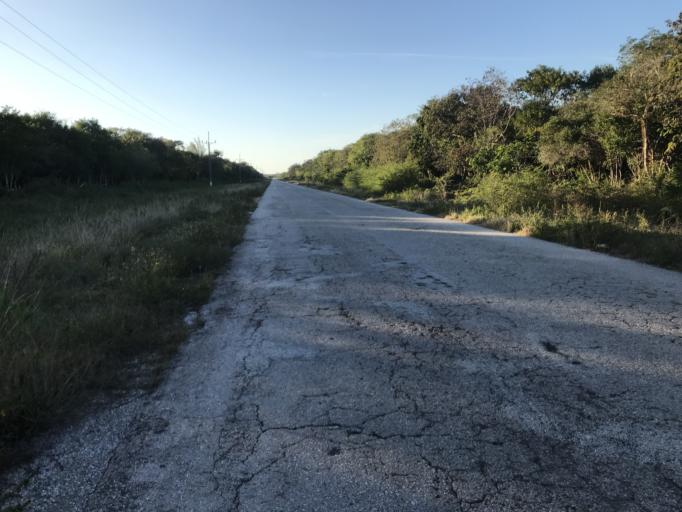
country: CU
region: Cienfuegos
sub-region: Municipio de Aguada de Pasajeros
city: Aguada de Pasajeros
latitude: 22.0764
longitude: -81.0628
